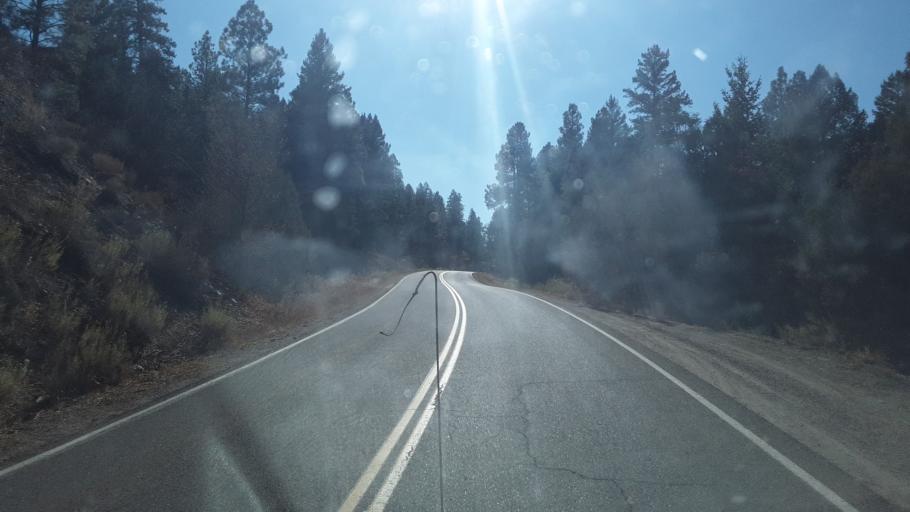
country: US
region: Colorado
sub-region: La Plata County
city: Durango
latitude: 37.4180
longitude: -107.8028
